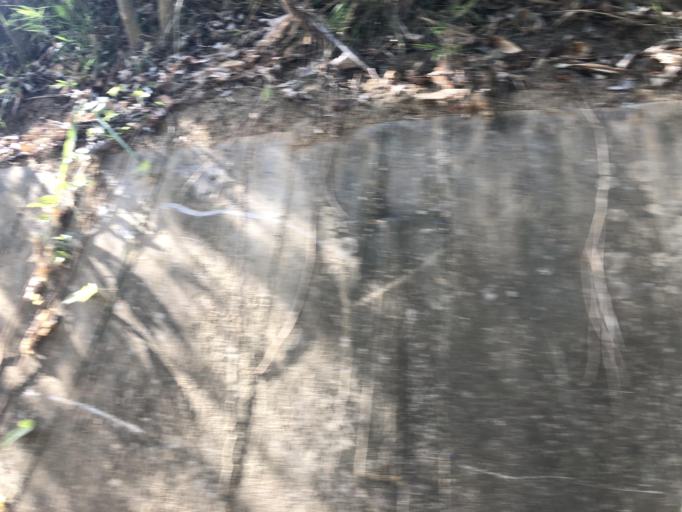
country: TW
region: Taiwan
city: Yujing
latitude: 23.0198
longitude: 120.3837
